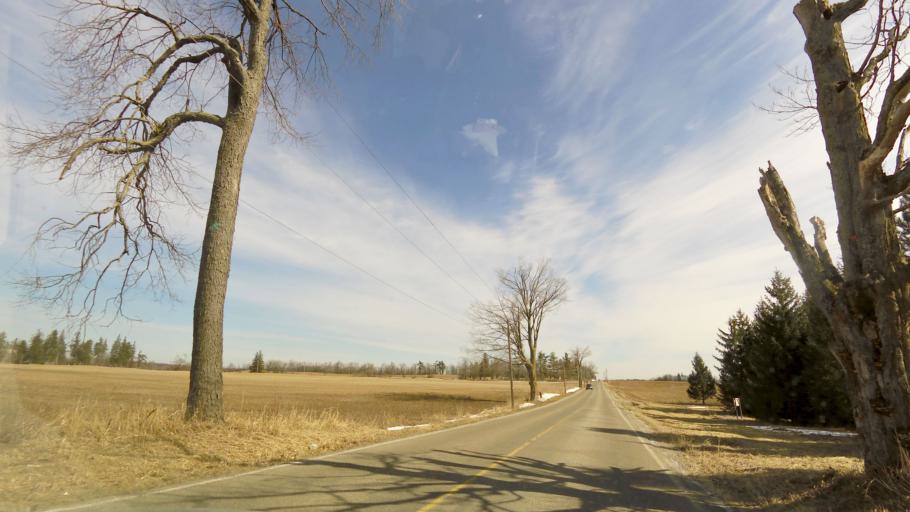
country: CA
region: Ontario
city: Burlington
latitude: 43.4005
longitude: -79.9356
